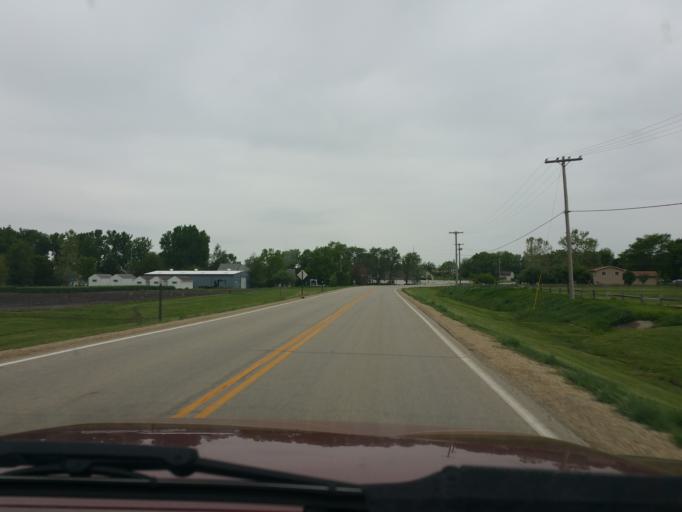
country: US
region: Kansas
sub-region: Riley County
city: Manhattan
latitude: 39.2308
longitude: -96.5787
